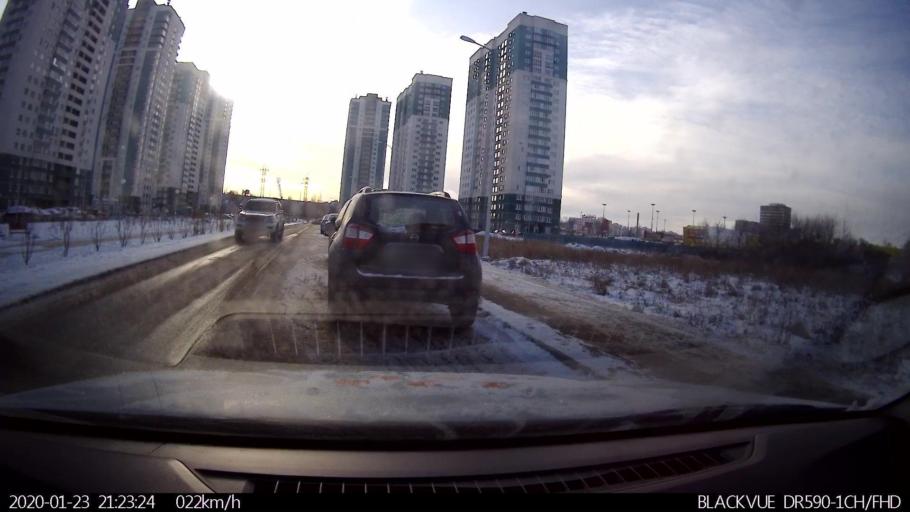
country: RU
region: Nizjnij Novgorod
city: Nizhniy Novgorod
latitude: 56.3032
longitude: 43.9510
